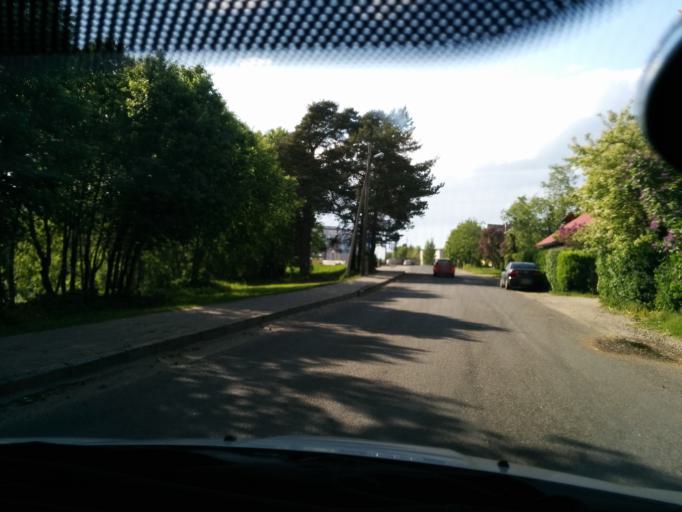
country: EE
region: Harju
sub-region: Loksa linn
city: Loksa
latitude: 59.5837
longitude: 25.7156
